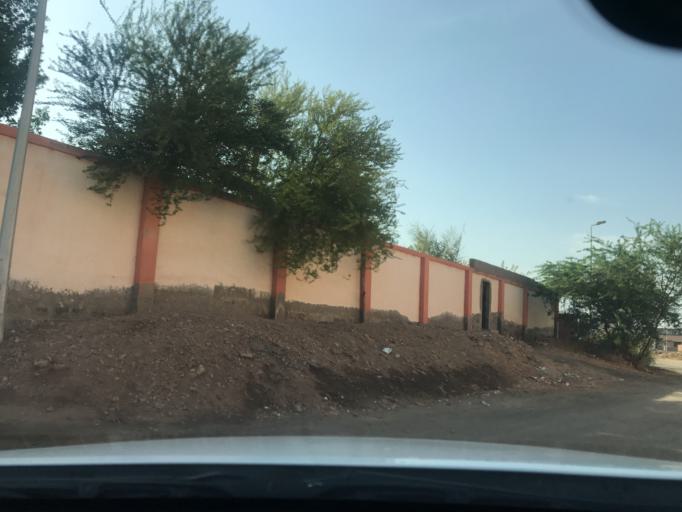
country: SA
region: Makkah
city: Al Jumum
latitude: 21.4479
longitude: 39.5347
